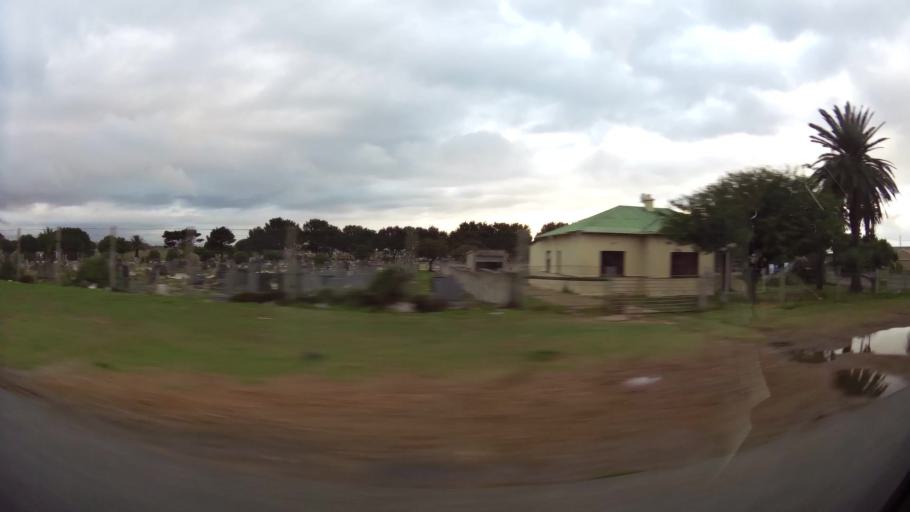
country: ZA
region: Eastern Cape
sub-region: Nelson Mandela Bay Metropolitan Municipality
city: Port Elizabeth
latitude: -33.9243
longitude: 25.6063
